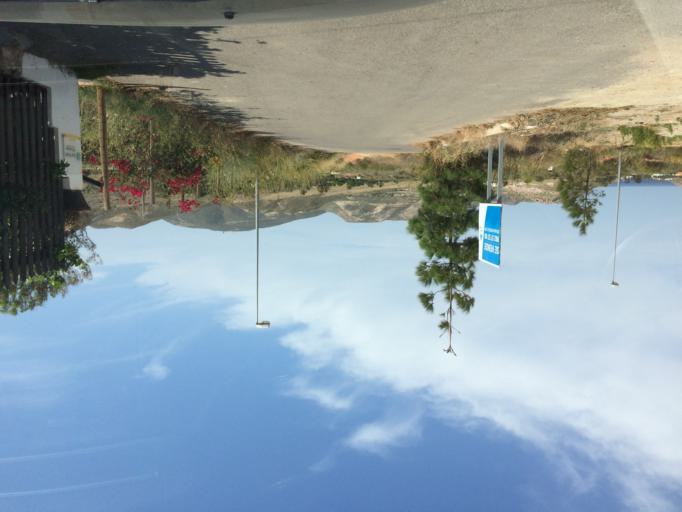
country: ES
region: Andalusia
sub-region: Provincia de Almeria
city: San Jose
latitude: 36.8468
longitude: -2.0380
